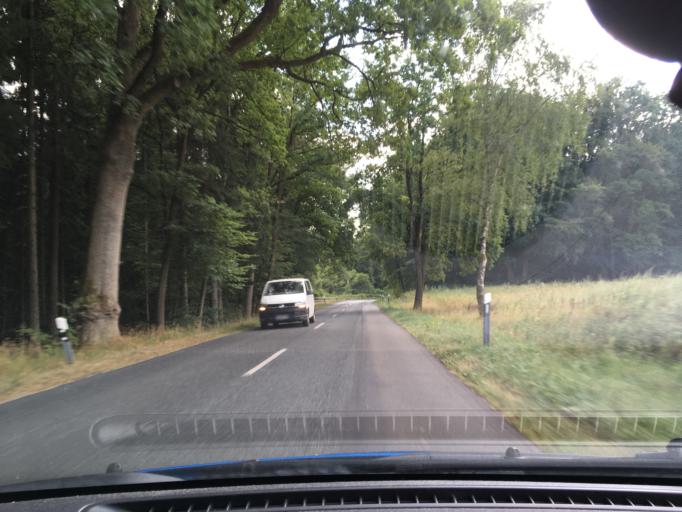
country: DE
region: Lower Saxony
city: Rehlingen
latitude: 53.0974
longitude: 10.2121
